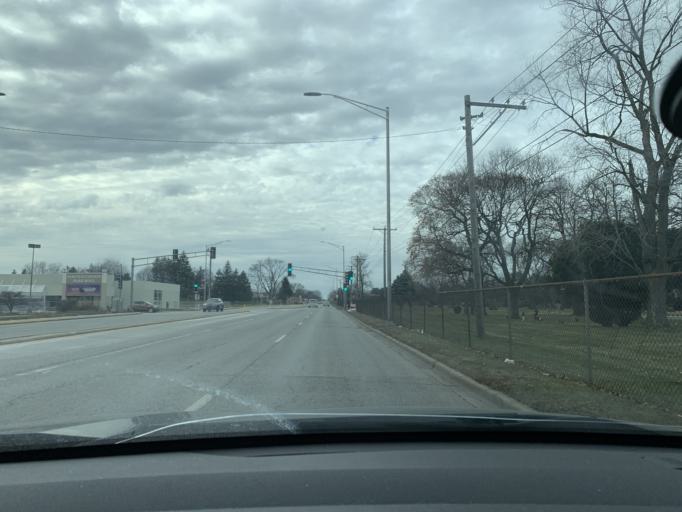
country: US
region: Illinois
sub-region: Cook County
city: North Riverside
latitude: 41.8501
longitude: -87.8155
